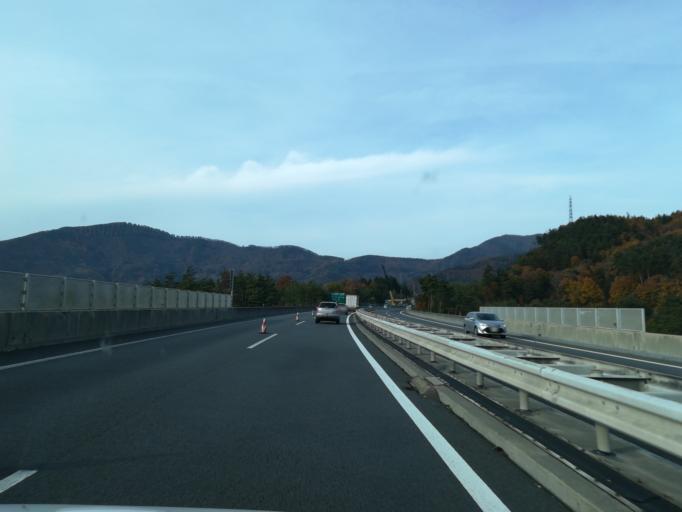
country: JP
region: Nagano
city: Ueda
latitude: 36.4611
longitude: 138.1984
